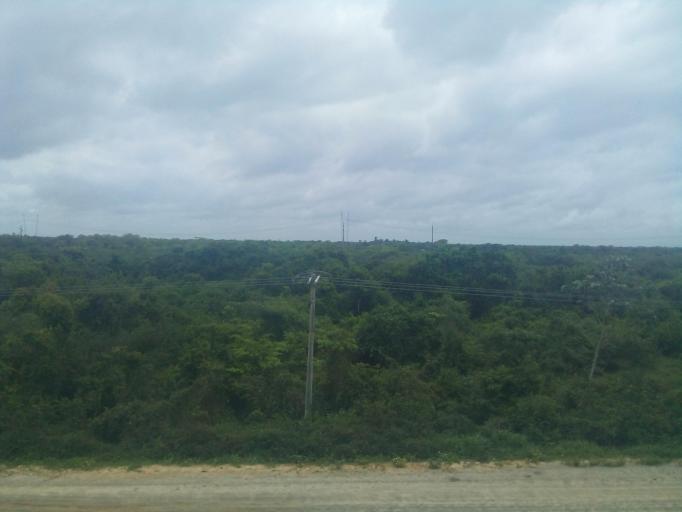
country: BR
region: Maranhao
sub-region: Arari
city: Arari
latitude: -3.5761
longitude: -44.7466
